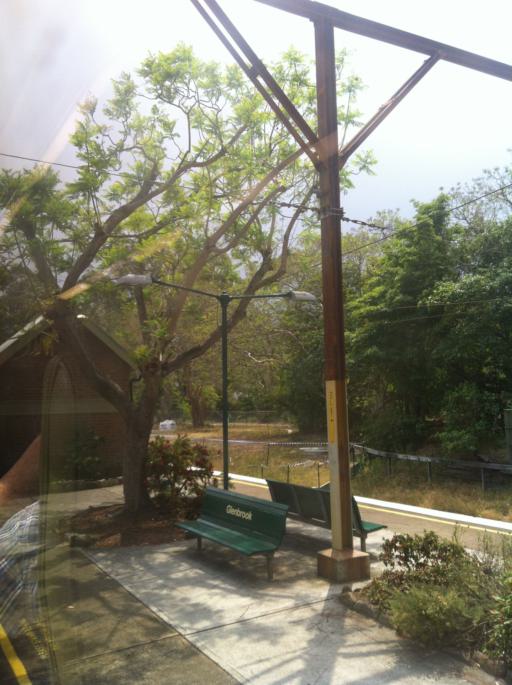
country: AU
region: New South Wales
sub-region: Blue Mountains Municipality
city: Glenbrook
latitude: -33.7690
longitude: 150.6203
